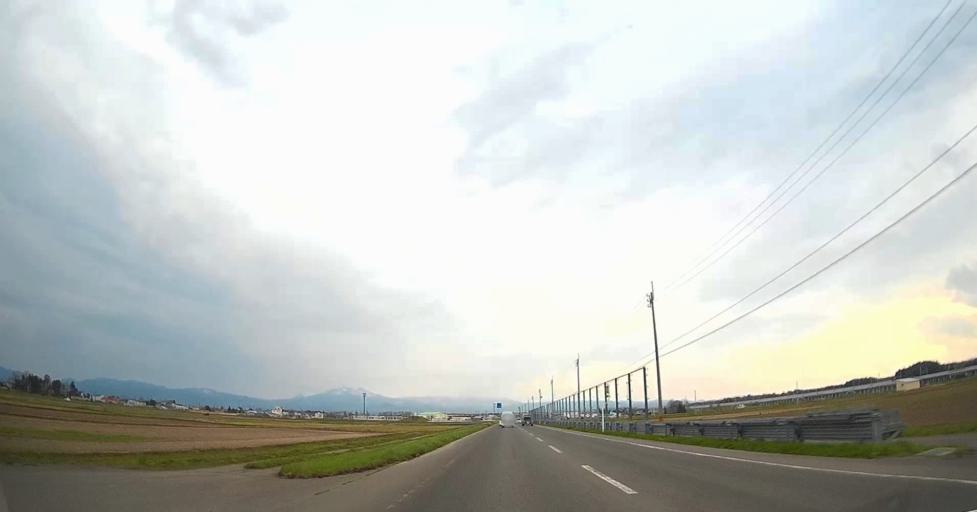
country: JP
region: Aomori
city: Aomori Shi
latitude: 40.8667
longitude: 140.6787
